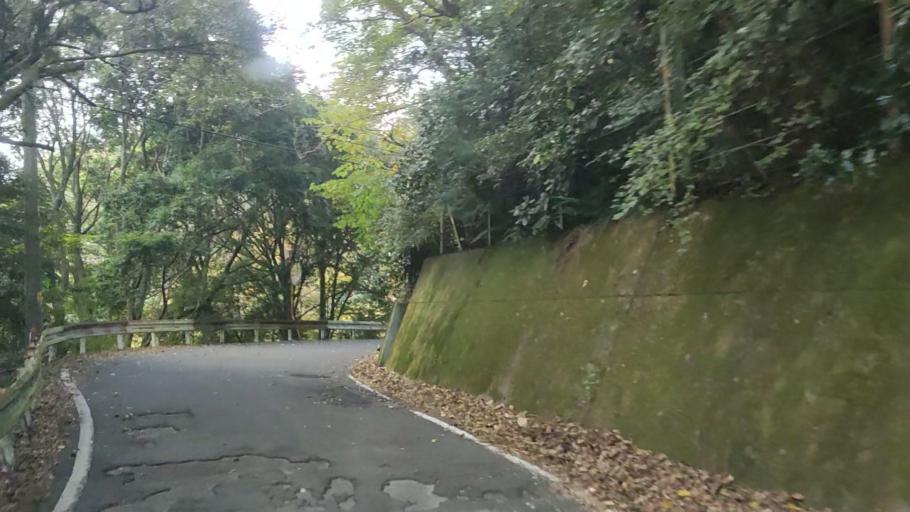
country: JP
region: Shizuoka
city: Ito
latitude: 34.9536
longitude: 139.0753
